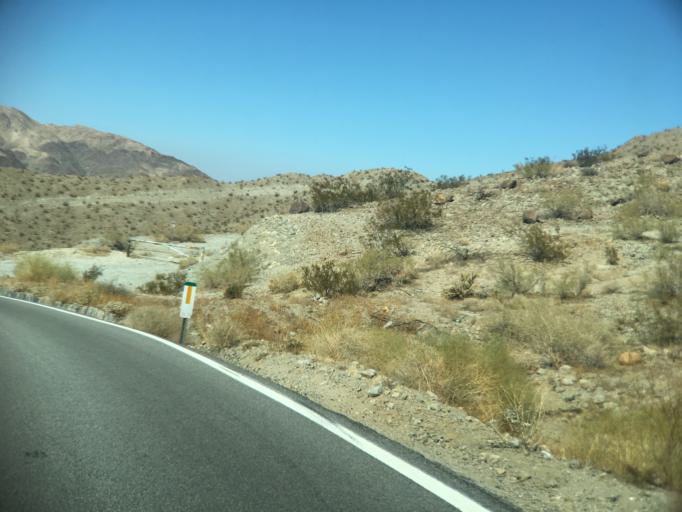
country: US
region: California
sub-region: Riverside County
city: Palm Desert
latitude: 33.6634
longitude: -116.3990
